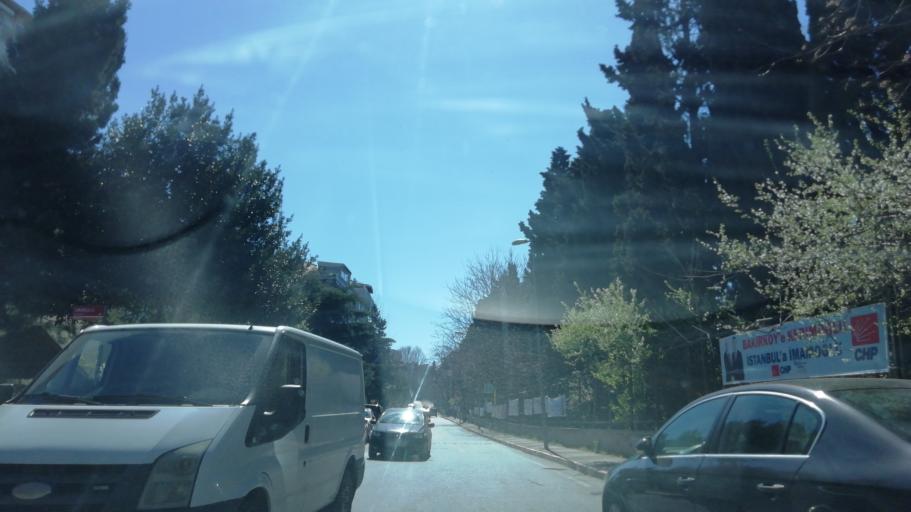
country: TR
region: Istanbul
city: Bahcelievler
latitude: 40.9859
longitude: 28.8665
